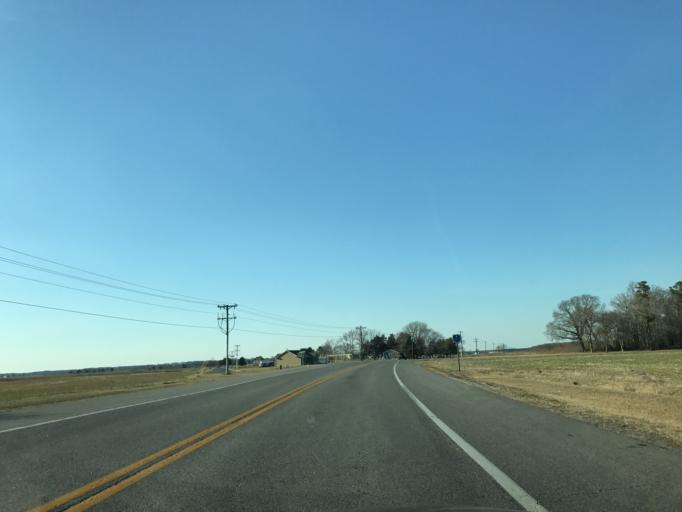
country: US
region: Maryland
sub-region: Caroline County
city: Greensboro
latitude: 39.0698
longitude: -75.8555
